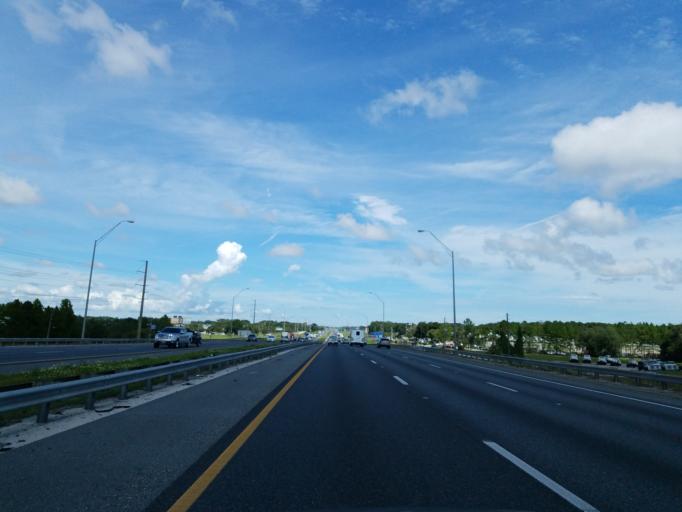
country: US
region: Florida
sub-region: Marion County
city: Ocala
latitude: 29.1690
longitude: -82.1848
